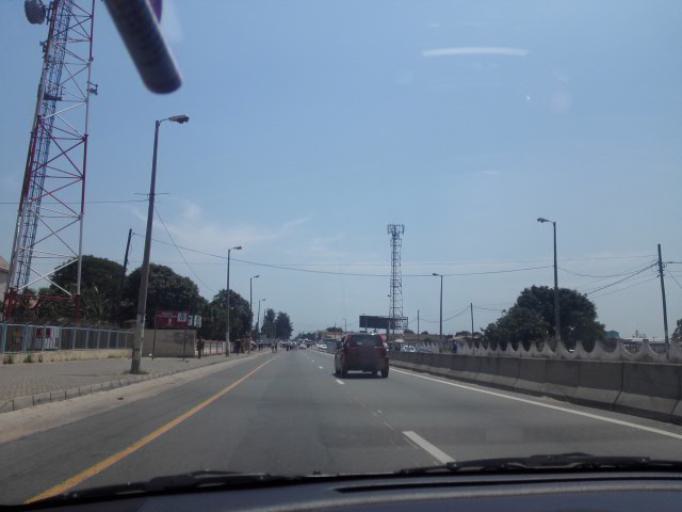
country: MZ
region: Maputo City
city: Maputo
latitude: -25.9365
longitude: 32.5485
